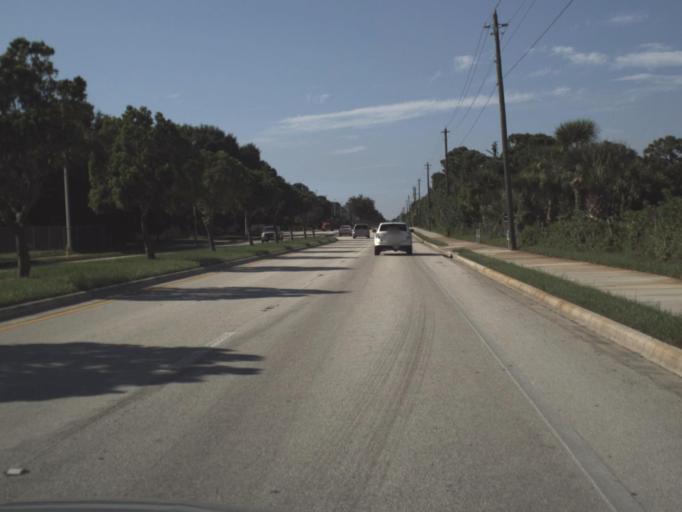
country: US
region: Florida
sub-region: Sarasota County
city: Englewood
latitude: 26.9863
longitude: -82.3643
